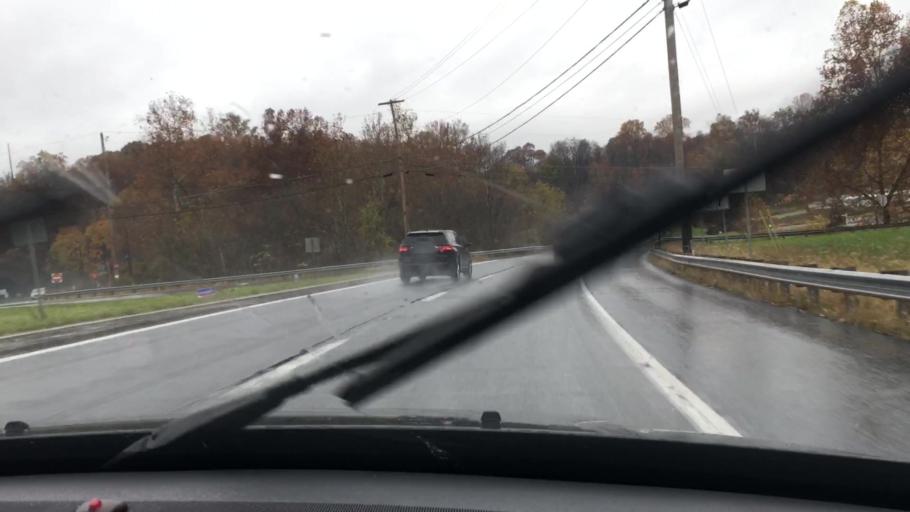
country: US
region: Pennsylvania
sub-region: Lancaster County
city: Willow Street
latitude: 39.9285
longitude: -76.2529
